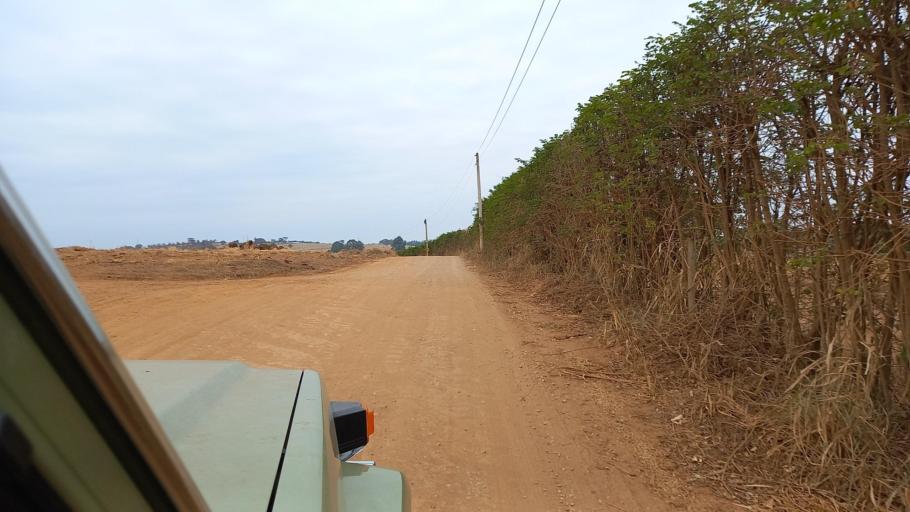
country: BR
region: Sao Paulo
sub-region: Moji-Guacu
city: Mogi-Gaucu
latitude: -22.2793
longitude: -46.8453
